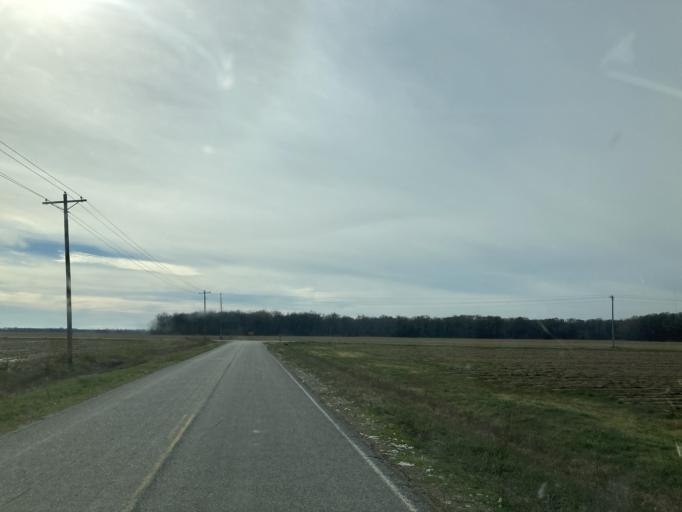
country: US
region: Mississippi
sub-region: Humphreys County
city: Belzoni
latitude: 33.0642
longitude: -90.6155
